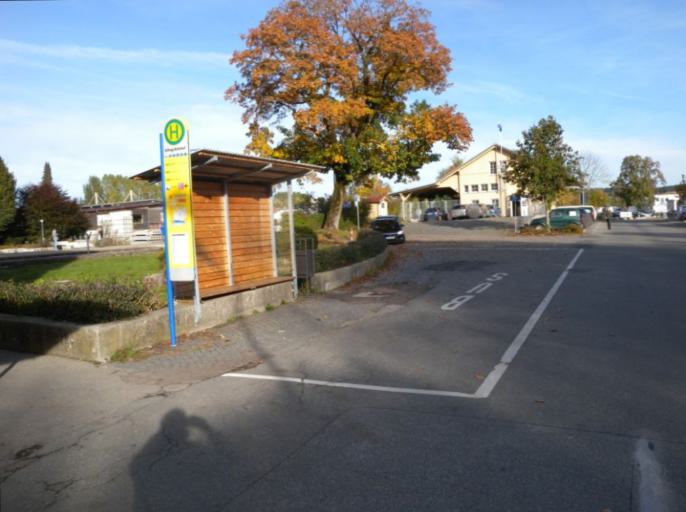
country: DE
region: Baden-Wuerttemberg
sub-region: Tuebingen Region
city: Kisslegg
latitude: 47.7933
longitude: 9.8822
